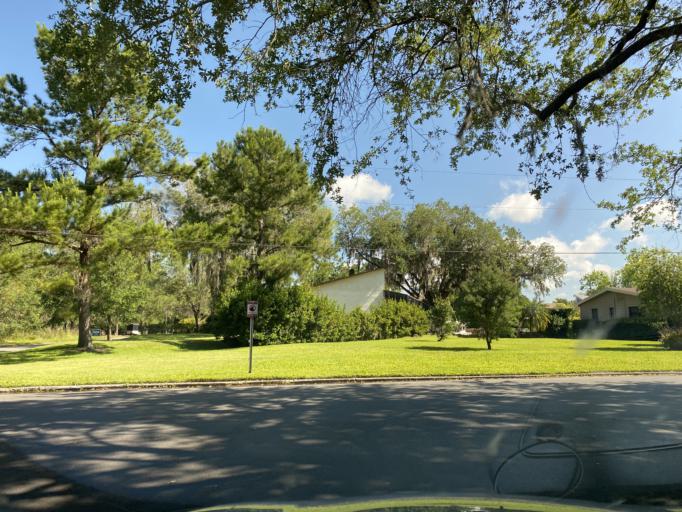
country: US
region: Florida
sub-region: Volusia County
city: DeBary
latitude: 28.8372
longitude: -81.3355
